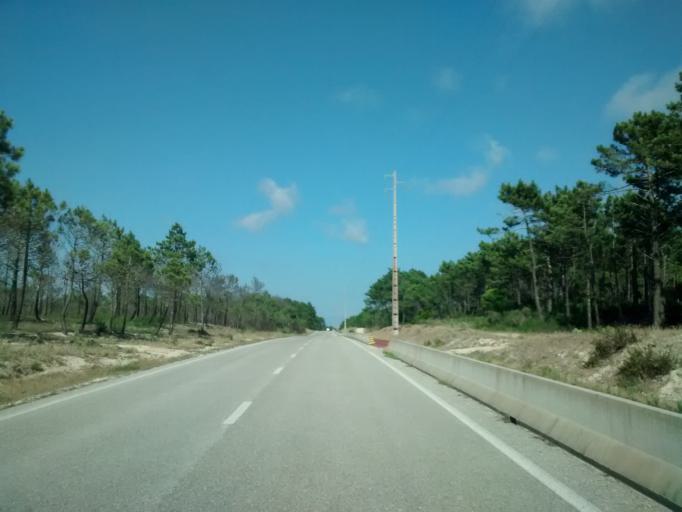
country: PT
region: Coimbra
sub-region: Figueira da Foz
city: Lavos
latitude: 40.0006
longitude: -8.8992
